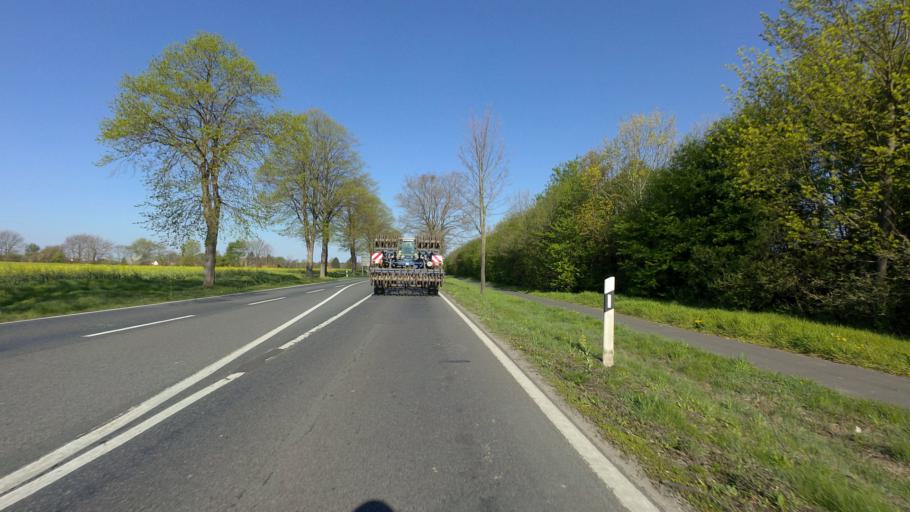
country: DE
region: Lower Saxony
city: Steimbke
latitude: 52.6541
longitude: 9.4021
